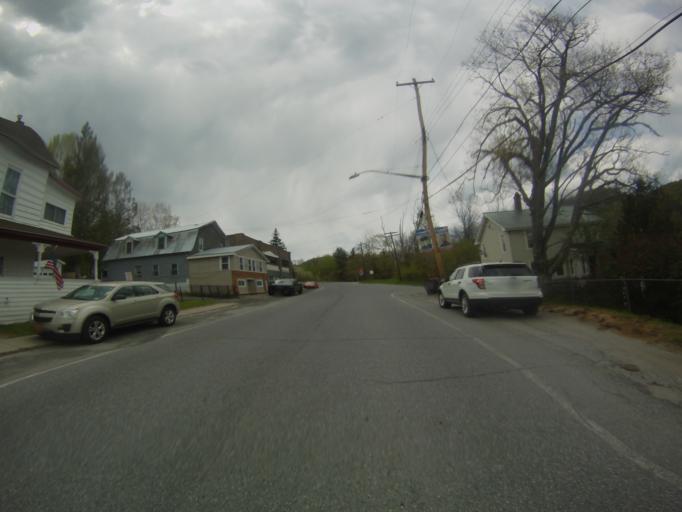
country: US
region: New York
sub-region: Essex County
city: Mineville
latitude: 44.0872
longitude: -73.5330
